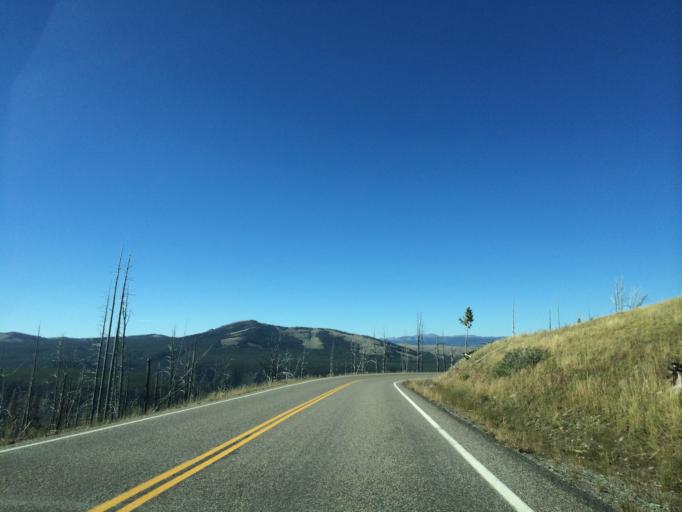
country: US
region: Montana
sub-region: Gallatin County
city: West Yellowstone
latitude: 44.8259
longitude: -110.4487
